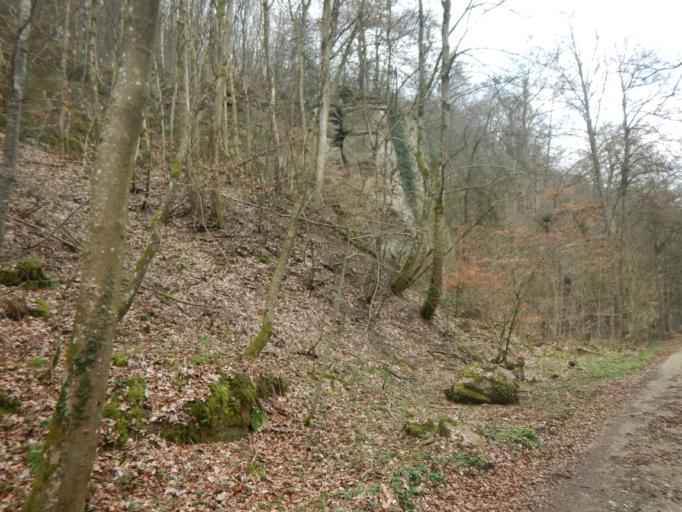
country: LU
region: Grevenmacher
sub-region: Canton d'Echternach
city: Beaufort
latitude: 49.8370
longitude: 6.3187
